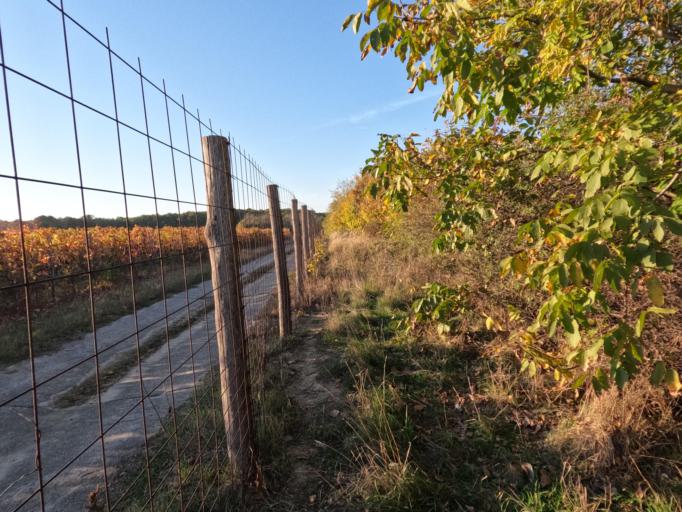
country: HU
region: Tolna
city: Szekszard
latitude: 46.3098
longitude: 18.6582
